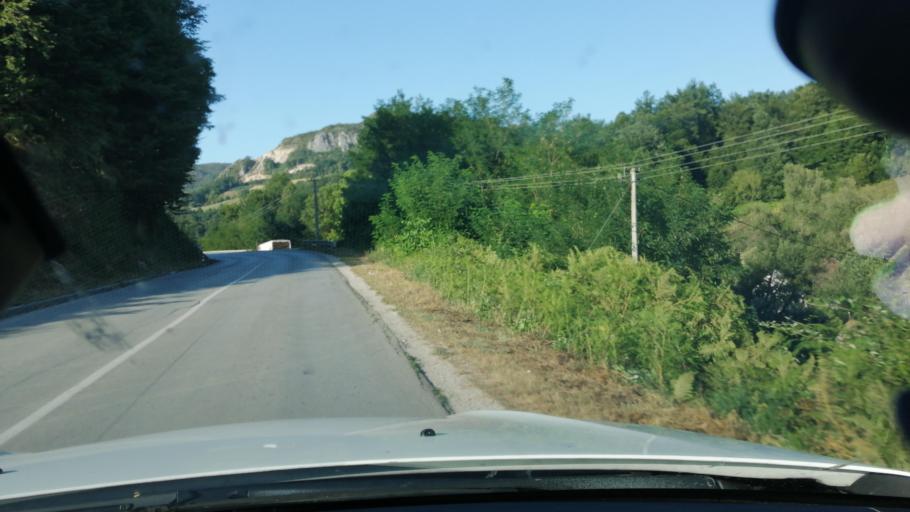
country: RS
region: Central Serbia
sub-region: Moravicki Okrug
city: Ivanjica
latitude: 43.6139
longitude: 20.2371
